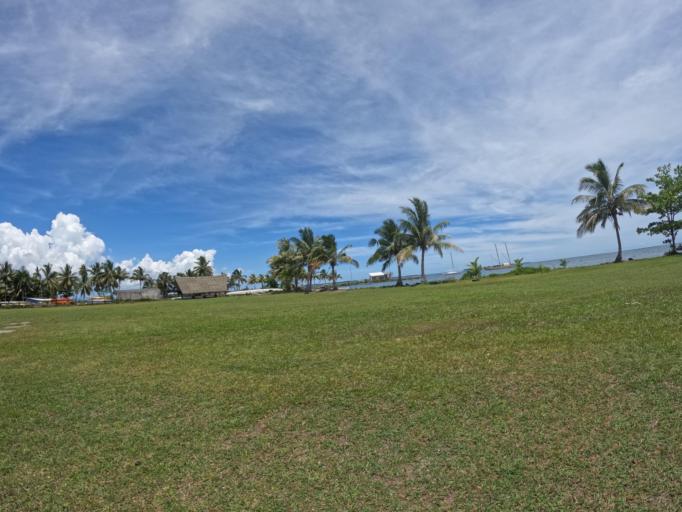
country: FJ
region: Central
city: Suva
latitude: -18.1503
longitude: 178.4538
